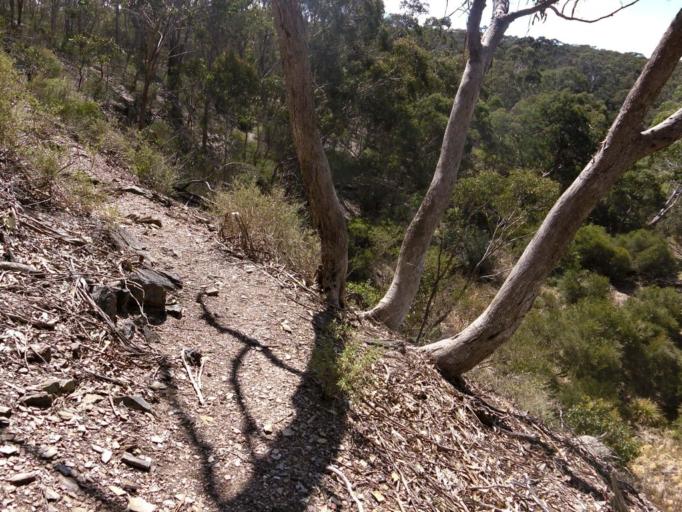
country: AU
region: Victoria
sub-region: Moorabool
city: Bacchus Marsh
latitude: -37.6571
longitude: 144.4982
